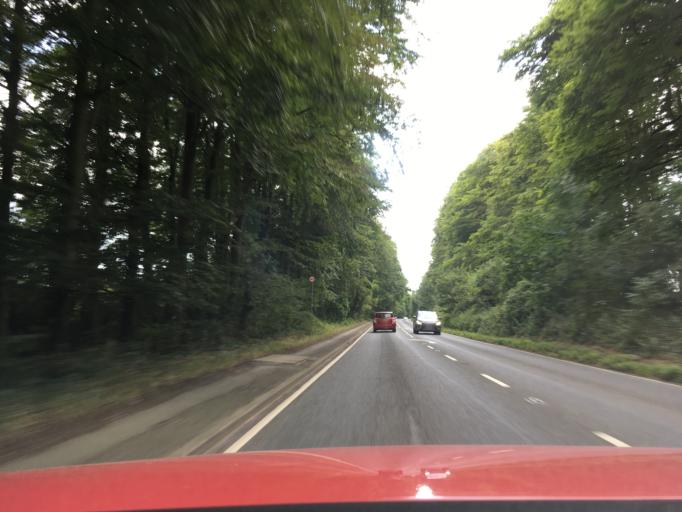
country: GB
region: England
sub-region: Hampshire
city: Compton
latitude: 51.0345
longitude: -1.3291
